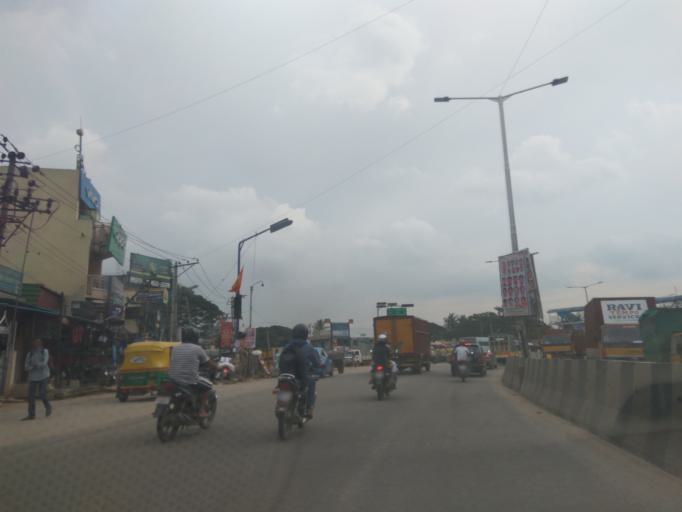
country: IN
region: Karnataka
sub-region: Bangalore Urban
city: Bangalore
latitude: 13.0086
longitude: 77.6962
